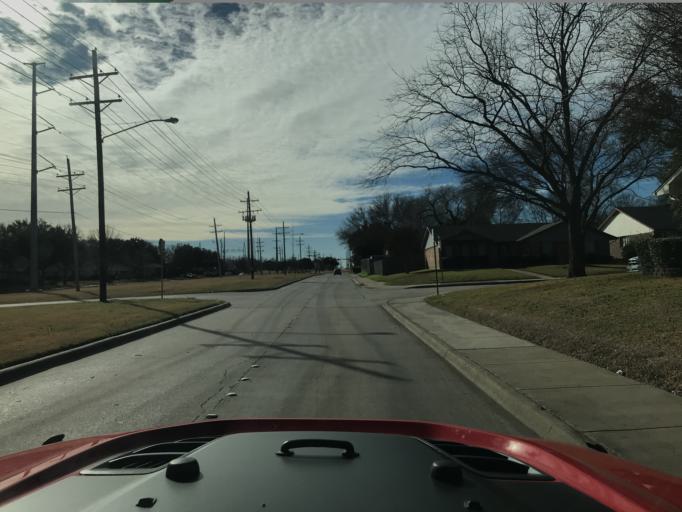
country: US
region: Texas
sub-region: Denton County
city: Highland Village
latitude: 33.0517
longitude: -97.0360
